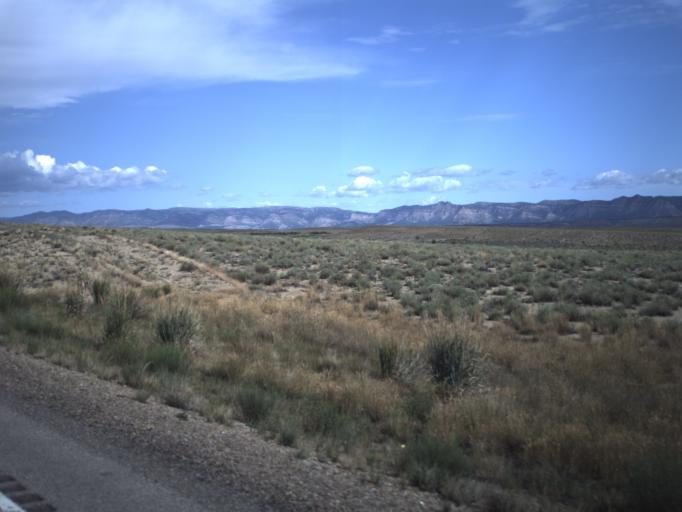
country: US
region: Utah
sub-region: Carbon County
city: Wellington
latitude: 39.5295
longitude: -110.5820
